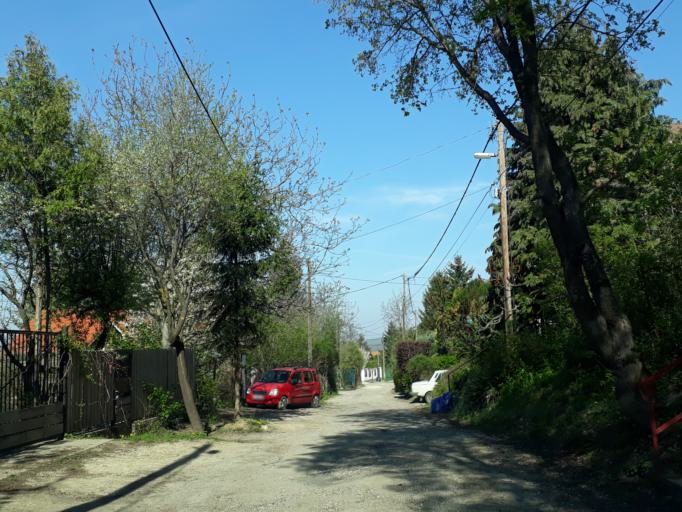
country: HU
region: Pest
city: Budakeszi
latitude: 47.5051
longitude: 18.9375
